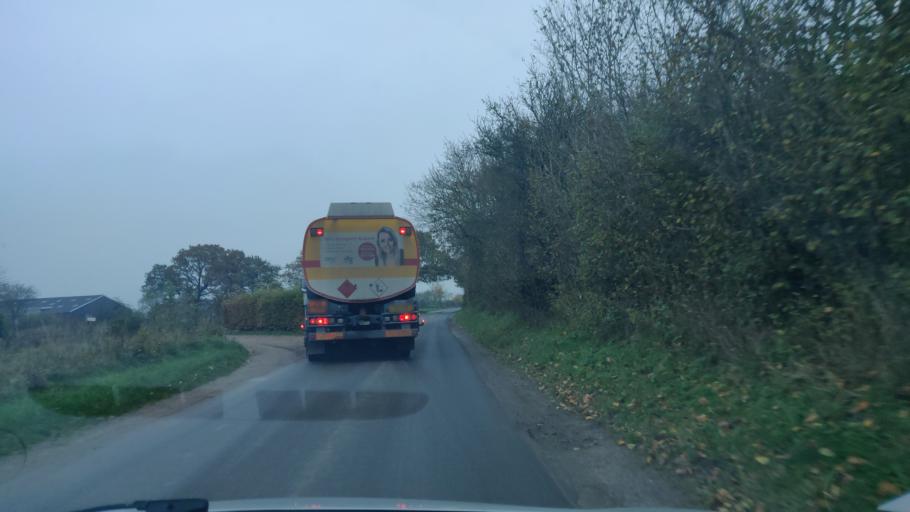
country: DK
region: South Denmark
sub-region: Kolding Kommune
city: Kolding
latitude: 55.5759
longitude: 9.4648
